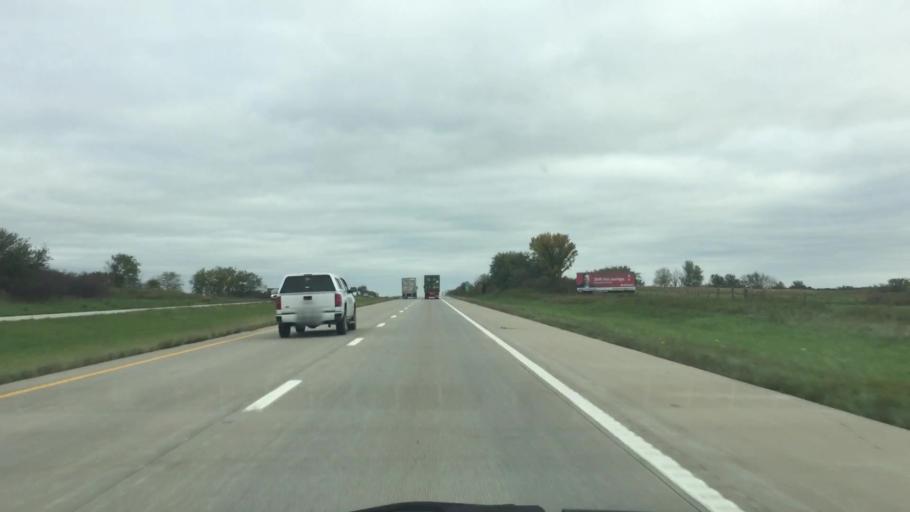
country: US
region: Missouri
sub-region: Clinton County
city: Cameron
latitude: 39.6405
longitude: -94.2423
